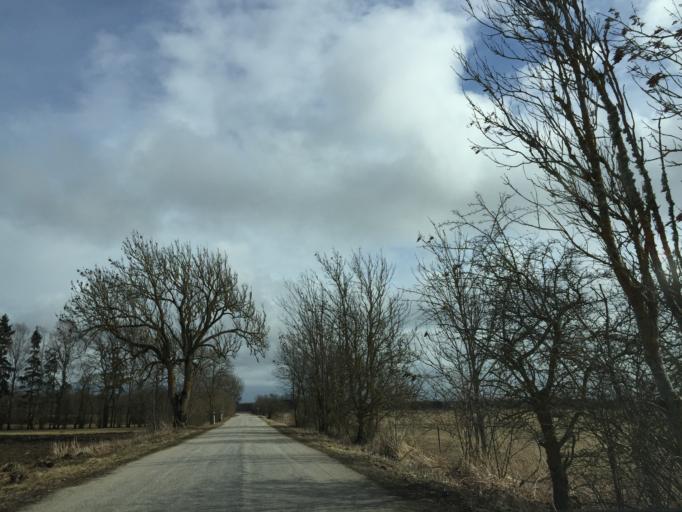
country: EE
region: Laeaene
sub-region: Lihula vald
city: Lihula
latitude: 58.7351
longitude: 23.8442
